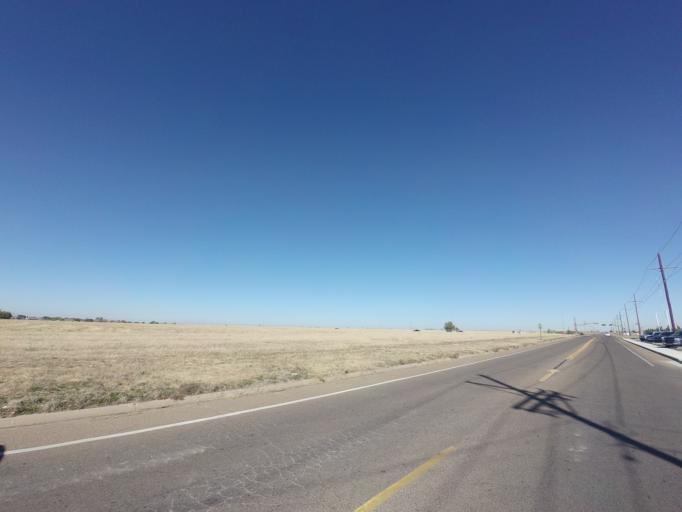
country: US
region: New Mexico
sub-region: Curry County
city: Clovis
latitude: 34.4322
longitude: -103.2143
